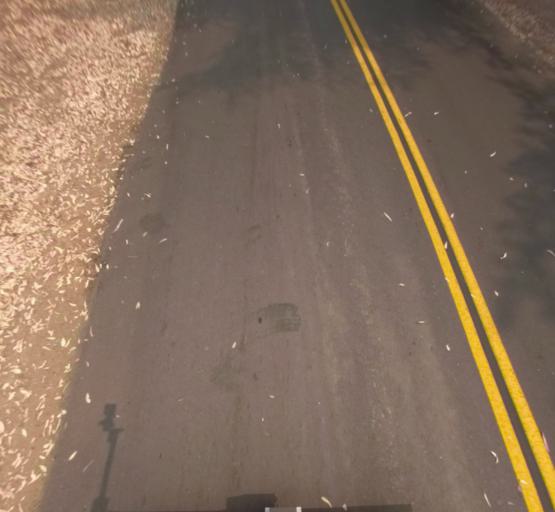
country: US
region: California
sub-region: Madera County
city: Madera Acres
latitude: 37.0277
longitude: -120.0632
